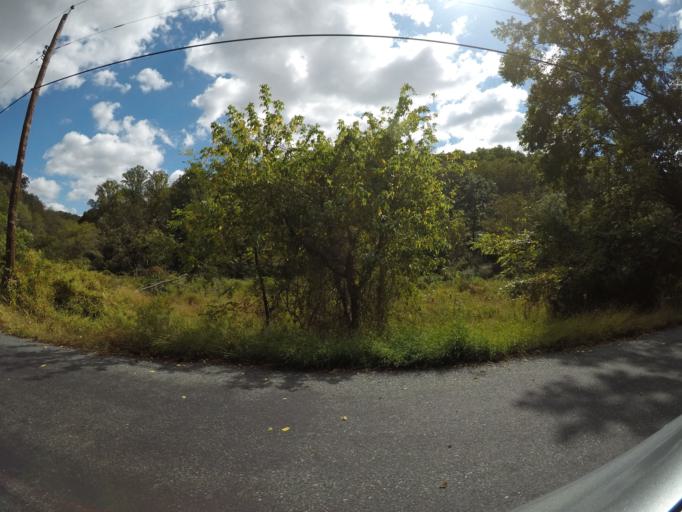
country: US
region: Maryland
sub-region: Harford County
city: Jarrettsville
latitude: 39.6830
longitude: -76.4857
